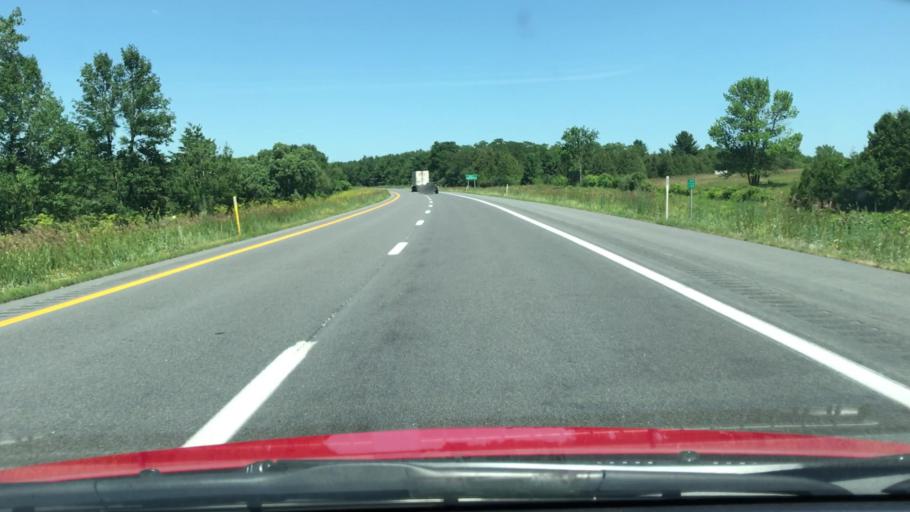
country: US
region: New York
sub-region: Clinton County
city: Cumberland Head
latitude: 44.7436
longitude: -73.4287
